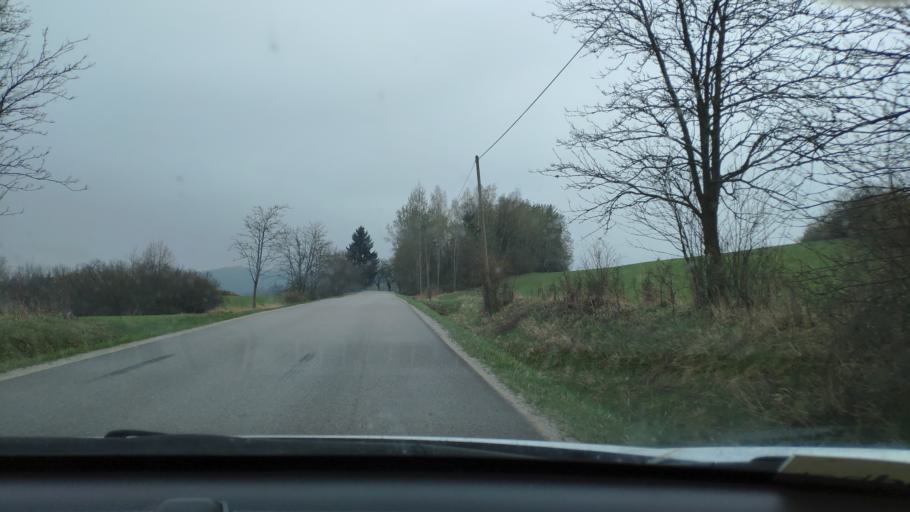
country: CZ
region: Vysocina
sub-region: Okres Jihlava
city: Telc
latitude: 49.1965
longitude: 15.3827
